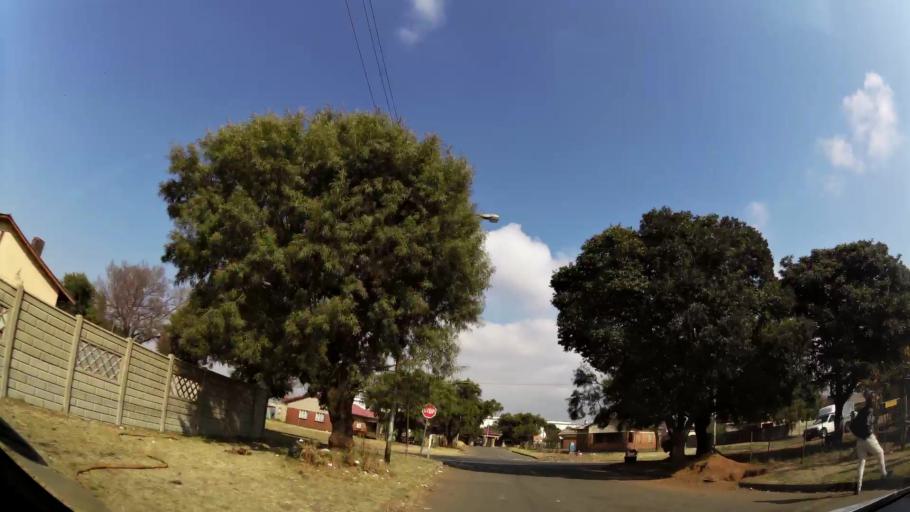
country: ZA
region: Gauteng
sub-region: Ekurhuleni Metropolitan Municipality
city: Germiston
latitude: -26.1612
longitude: 28.2007
